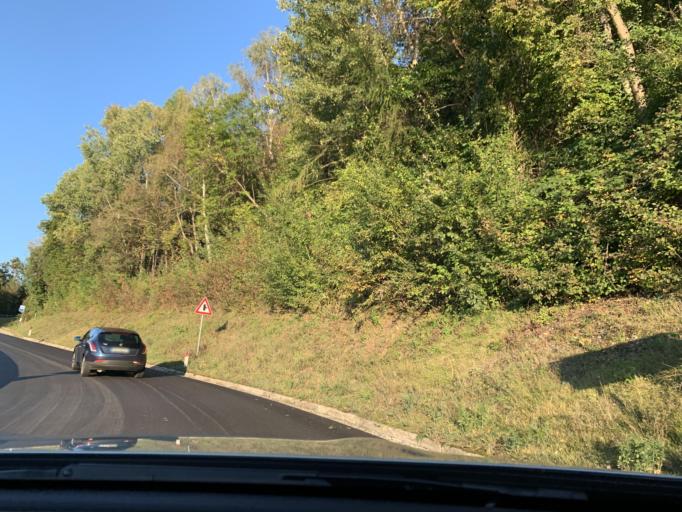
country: IT
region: Trentino-Alto Adige
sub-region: Bolzano
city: Fie Allo Sciliar
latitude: 46.4995
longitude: 11.4689
